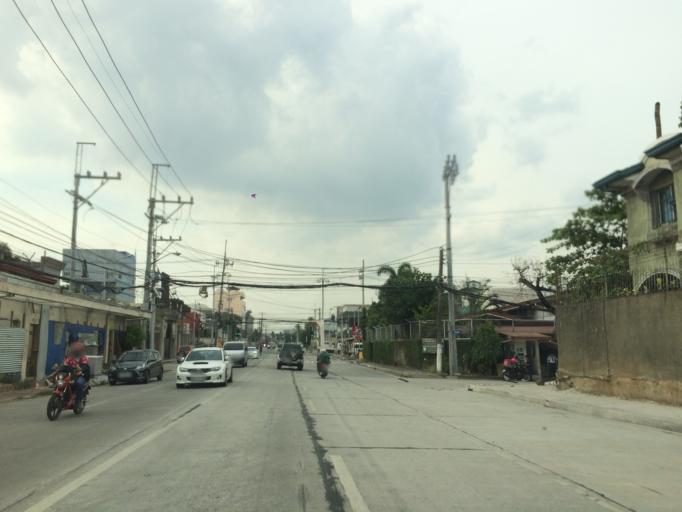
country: PH
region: Calabarzon
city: Del Monte
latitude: 14.6379
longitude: 121.0056
